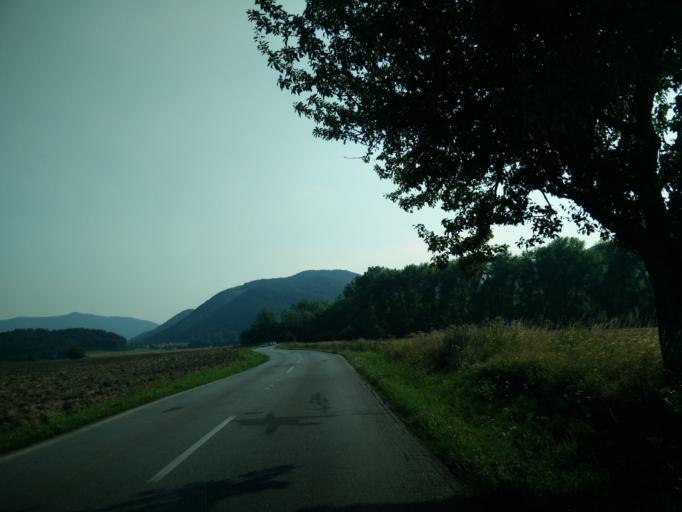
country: SK
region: Zilinsky
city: Rajec
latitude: 49.0580
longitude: 18.6250
